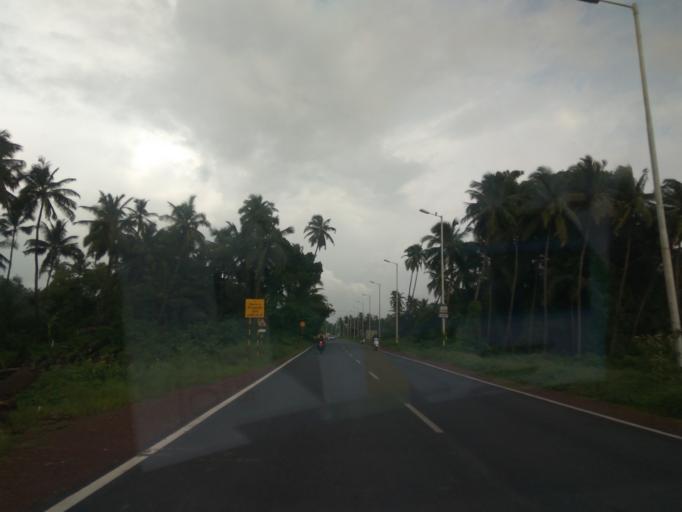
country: IN
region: Goa
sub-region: North Goa
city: Goa Velha
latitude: 15.4352
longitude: 73.8840
